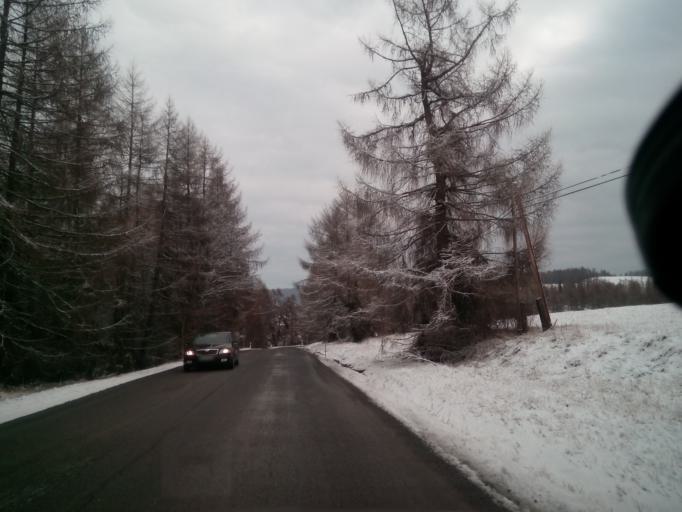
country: SK
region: Presovsky
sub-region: Okres Presov
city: Levoca
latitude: 49.0624
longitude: 20.6738
